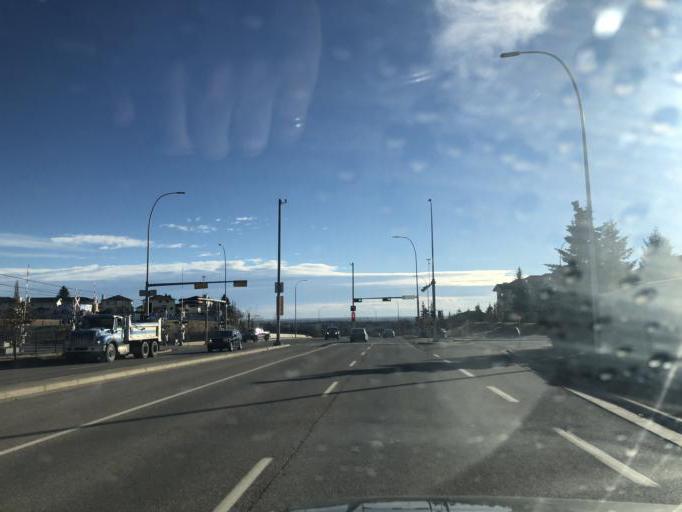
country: CA
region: Alberta
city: Calgary
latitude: 51.0371
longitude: -114.1799
